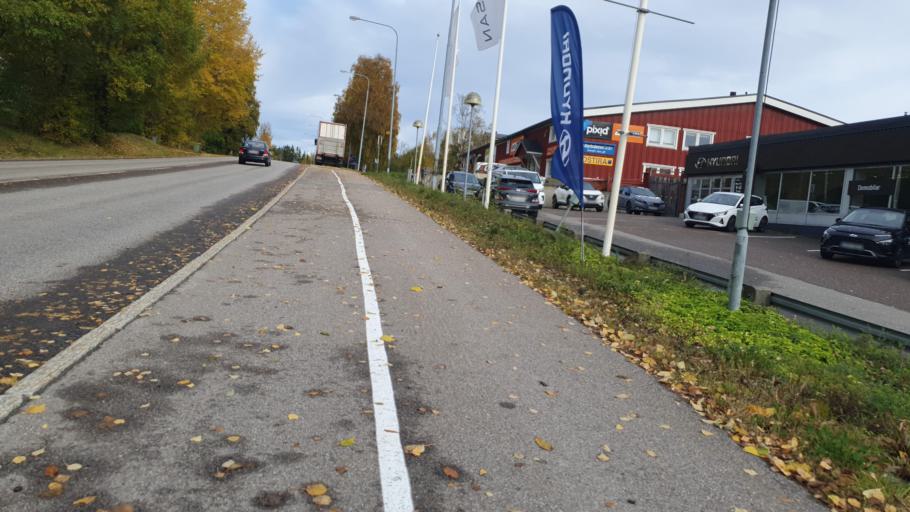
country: SE
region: Vaesternorrland
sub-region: Sundsvalls Kommun
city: Johannedal
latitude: 62.4257
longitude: 17.3468
